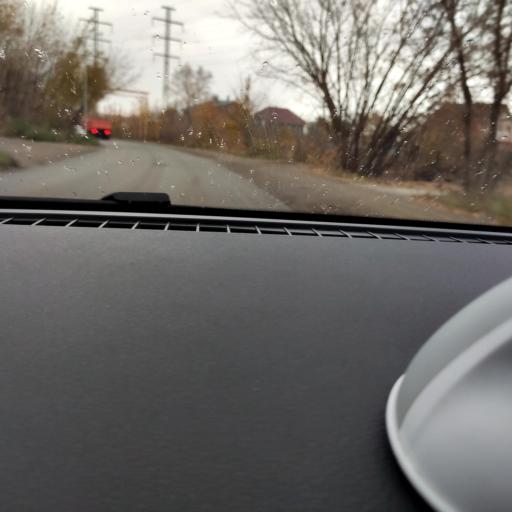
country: RU
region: Samara
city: Petra-Dubrava
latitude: 53.2945
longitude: 50.2924
